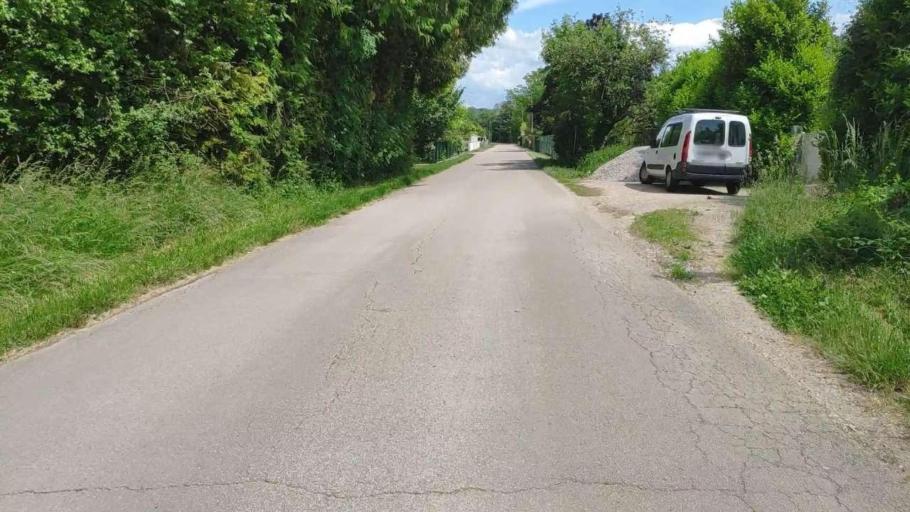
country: FR
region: Franche-Comte
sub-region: Departement du Jura
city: Bletterans
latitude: 46.7452
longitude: 5.4860
